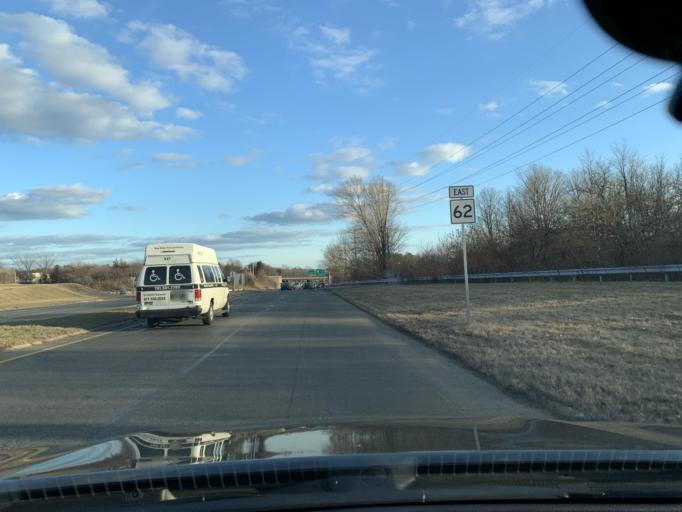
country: US
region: Massachusetts
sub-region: Essex County
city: Danvers
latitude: 42.5856
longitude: -70.9702
